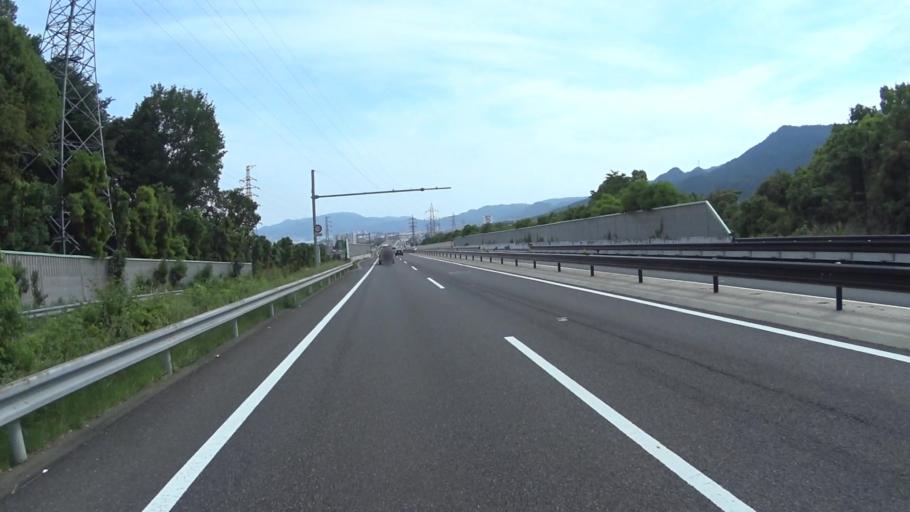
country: JP
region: Shiga Prefecture
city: Otsu-shi
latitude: 35.0794
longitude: 135.8815
